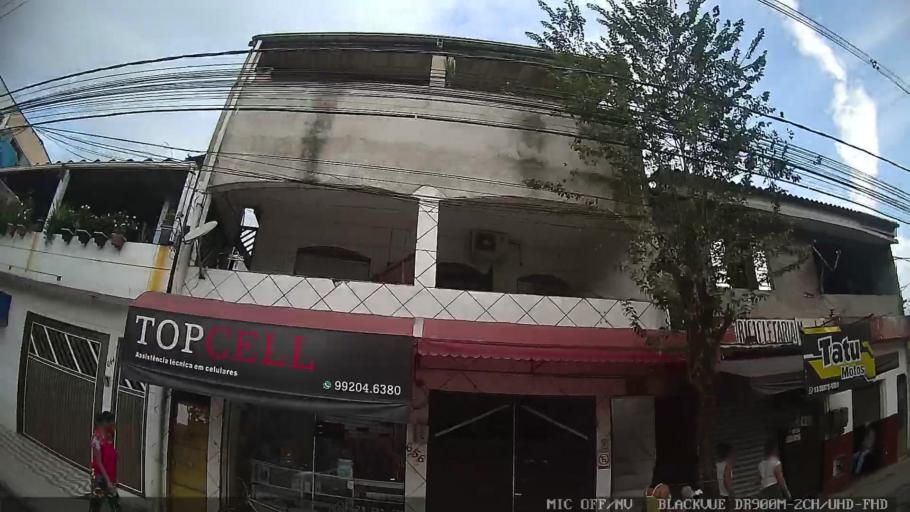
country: BR
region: Sao Paulo
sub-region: Cubatao
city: Cubatao
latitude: -23.8986
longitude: -46.4355
